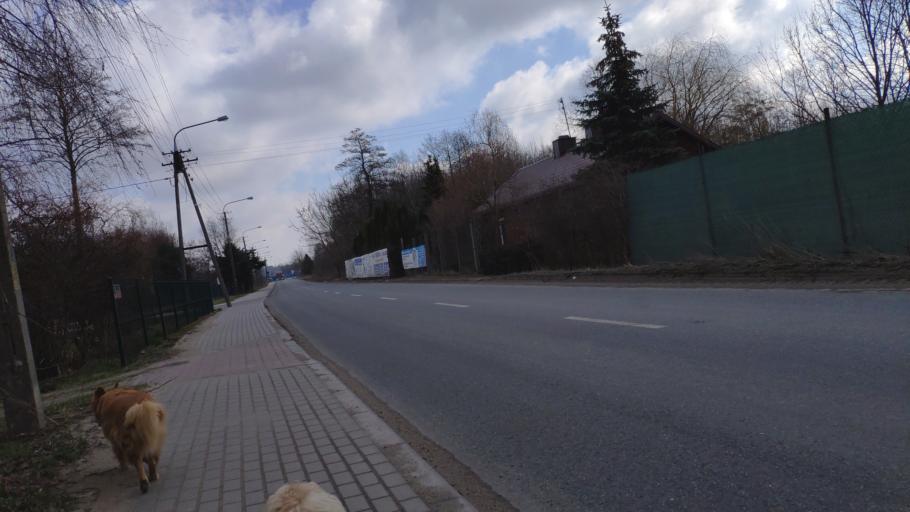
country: PL
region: Lodz Voivodeship
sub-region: Powiat pabianicki
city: Konstantynow Lodzki
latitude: 51.7346
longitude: 19.3598
